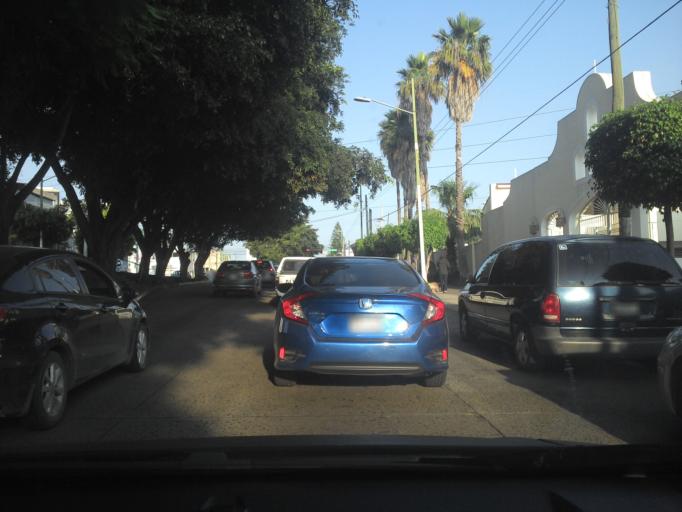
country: MX
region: Jalisco
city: Guadalajara
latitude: 20.6298
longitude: -103.4051
